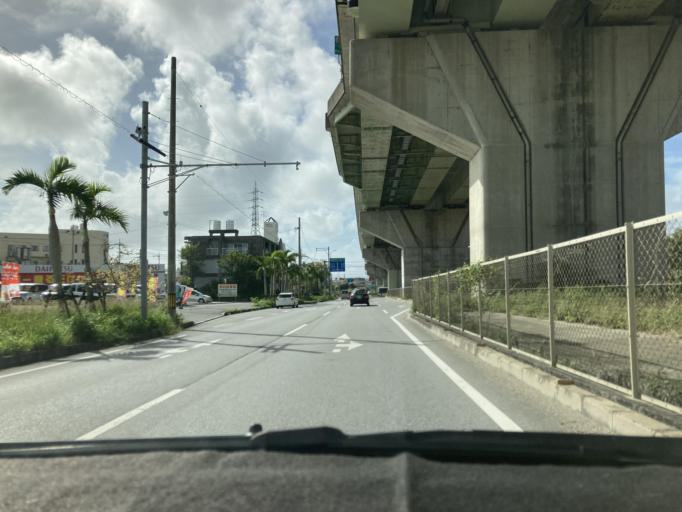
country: JP
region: Okinawa
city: Naha-shi
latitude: 26.2017
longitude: 127.7392
